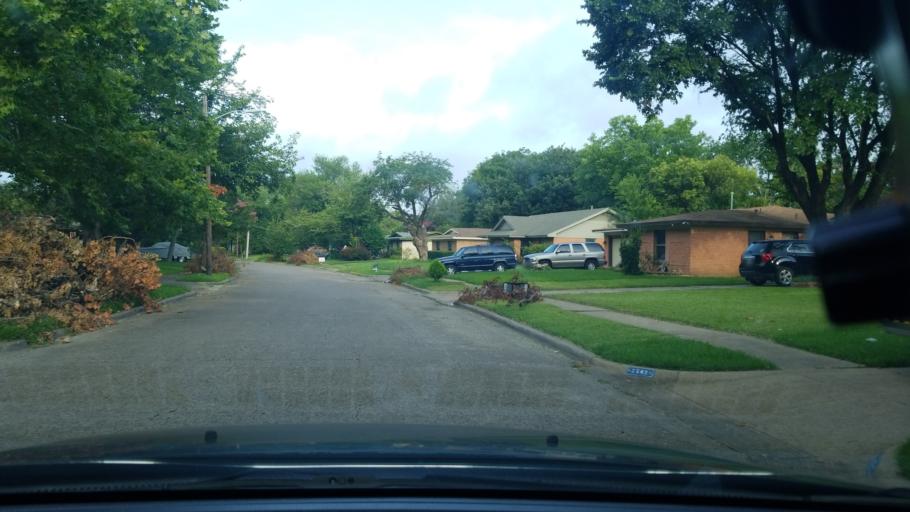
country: US
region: Texas
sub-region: Dallas County
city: Garland
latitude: 32.8295
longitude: -96.6704
